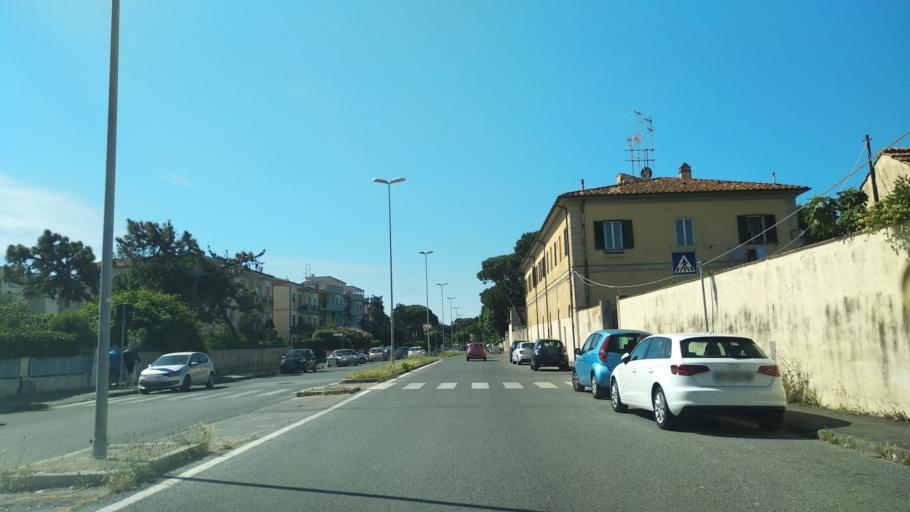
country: IT
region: Tuscany
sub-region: Provincia di Livorno
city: Livorno
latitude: 43.5217
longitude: 10.3167
